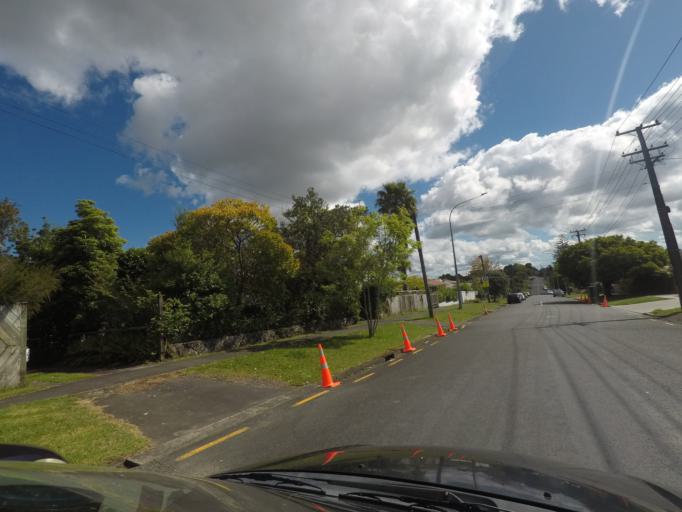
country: NZ
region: Auckland
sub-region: Auckland
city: Waitakere
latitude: -36.9139
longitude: 174.6660
